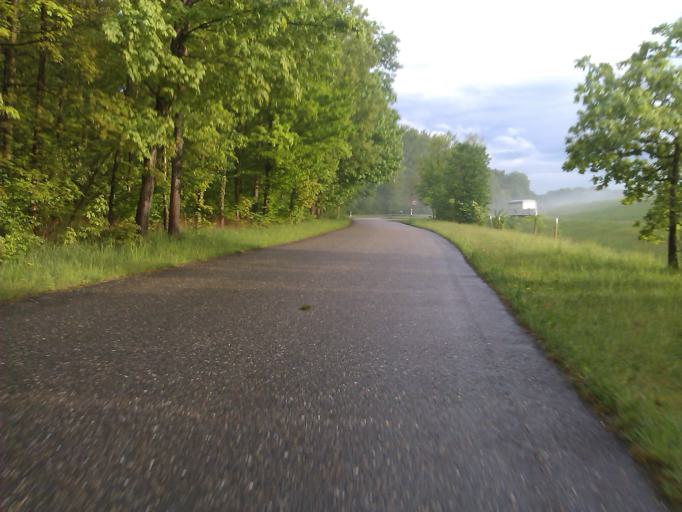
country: DE
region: Baden-Wuerttemberg
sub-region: Karlsruhe Region
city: Lichtenau
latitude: 48.7296
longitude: 7.9701
